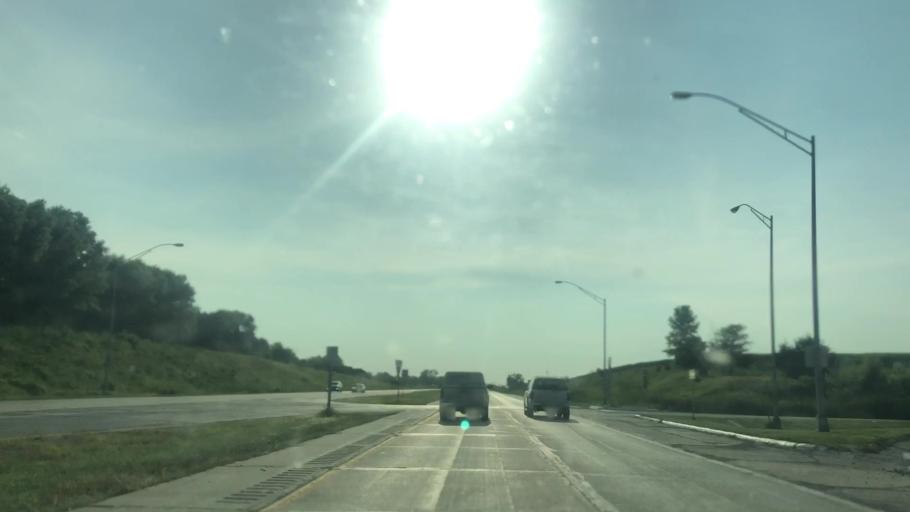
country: US
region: Iowa
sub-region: Story County
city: Nevada
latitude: 42.0057
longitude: -93.4526
